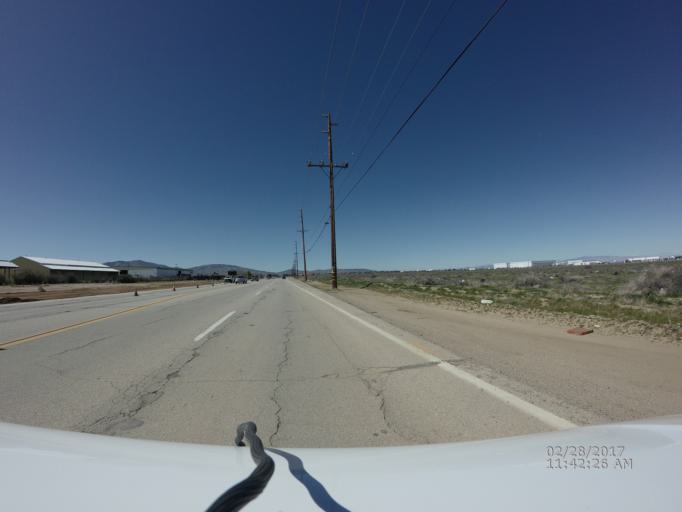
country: US
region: California
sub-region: Los Angeles County
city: Palmdale
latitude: 34.6022
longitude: -118.1040
